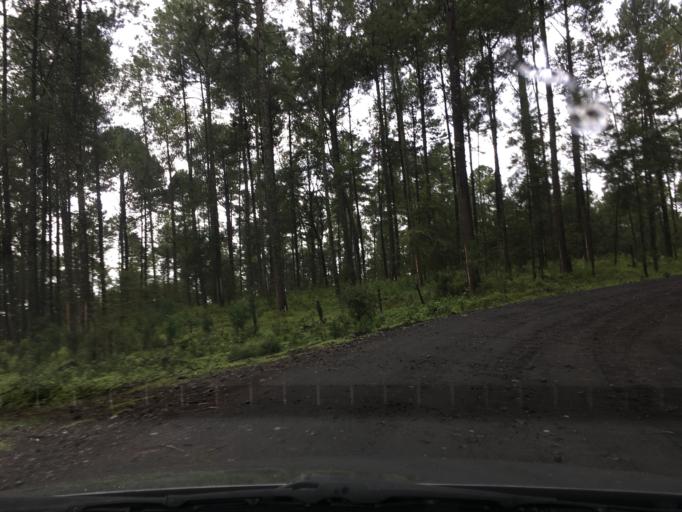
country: MX
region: Michoacan
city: Nuevo San Juan Parangaricutiro
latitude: 19.4459
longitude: -102.1791
